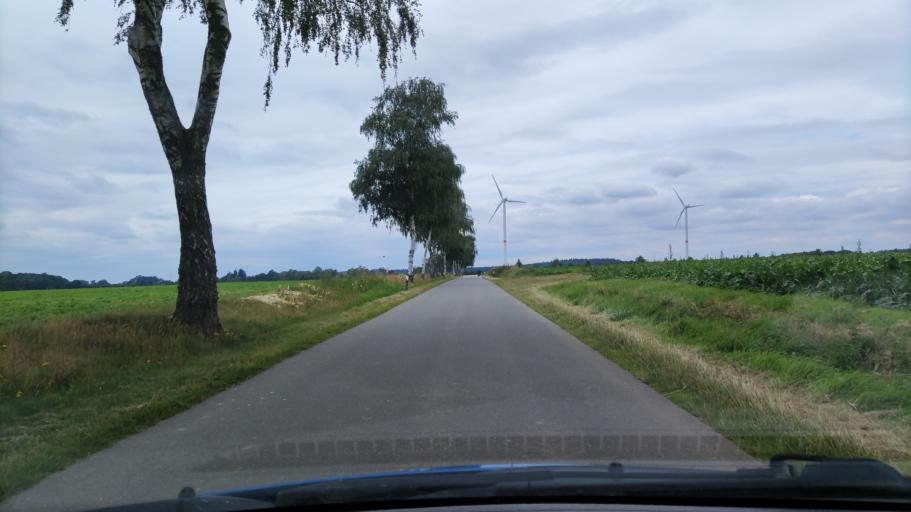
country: DE
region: Lower Saxony
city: Oetzen
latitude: 53.0218
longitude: 10.7006
